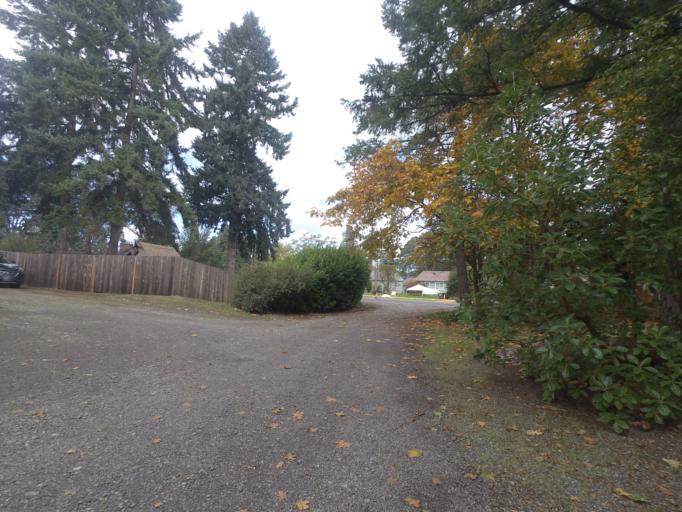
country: US
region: Washington
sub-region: Pierce County
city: Lakewood
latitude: 47.1748
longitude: -122.5254
